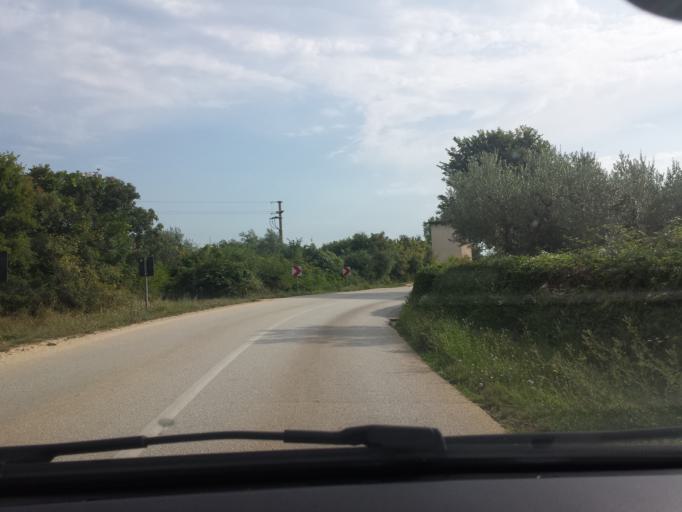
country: HR
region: Istarska
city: Galizana
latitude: 44.9232
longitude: 13.8615
